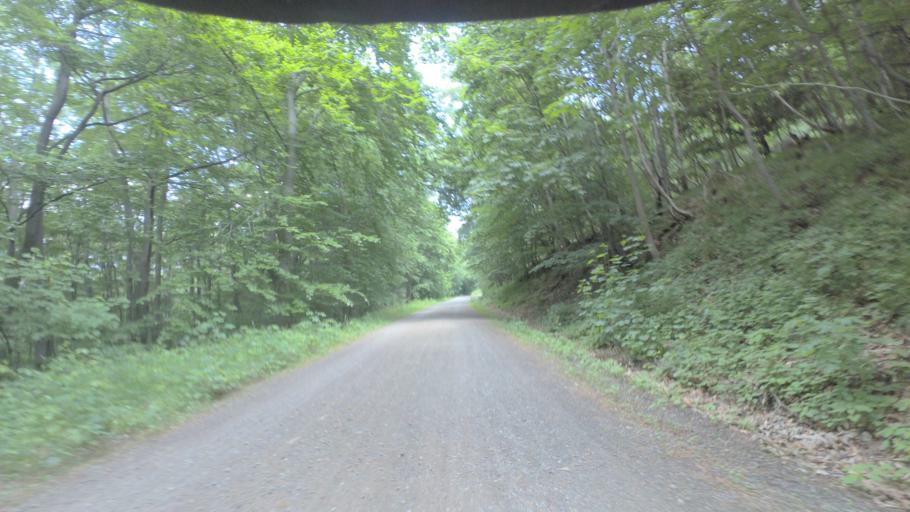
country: DE
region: Lower Saxony
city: Bad Harzburg
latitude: 51.8865
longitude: 10.5999
